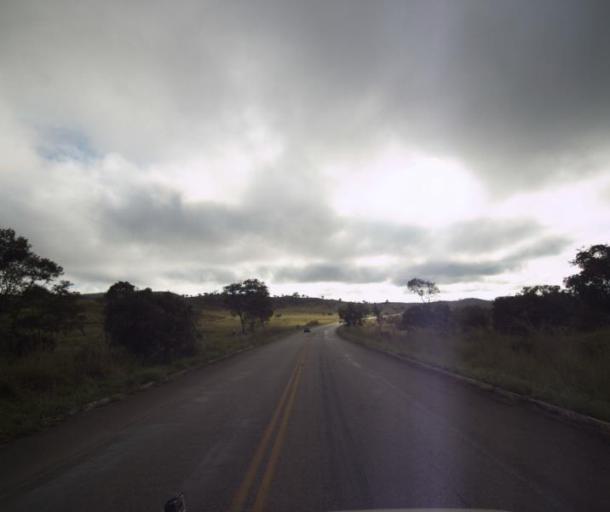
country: BR
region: Goias
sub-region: Pirenopolis
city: Pirenopolis
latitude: -15.7340
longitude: -48.7159
